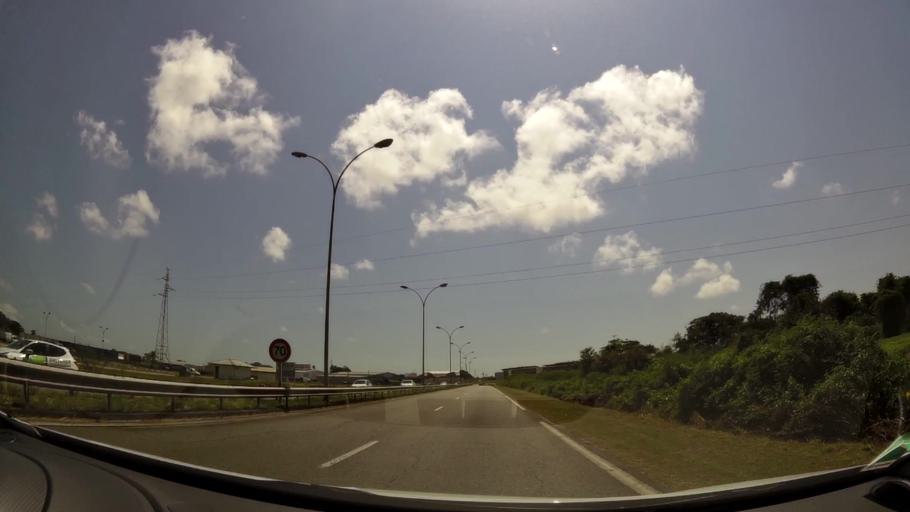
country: GF
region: Guyane
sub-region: Guyane
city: Cayenne
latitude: 4.9230
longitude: -52.3263
